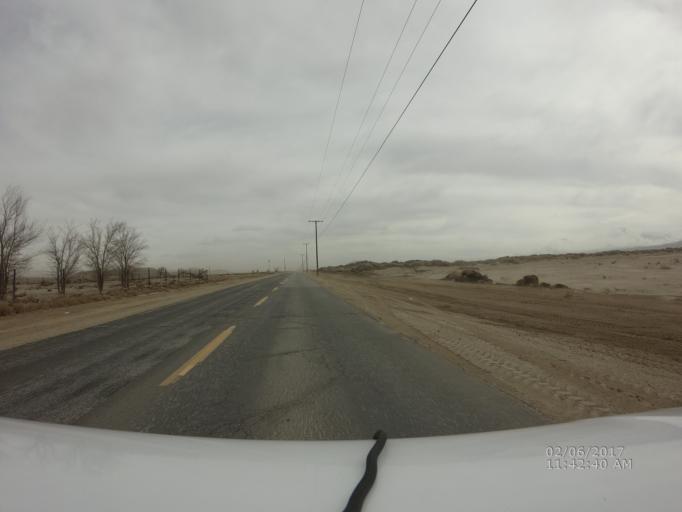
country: US
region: California
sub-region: Los Angeles County
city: Lake Los Angeles
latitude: 34.6019
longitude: -117.7006
